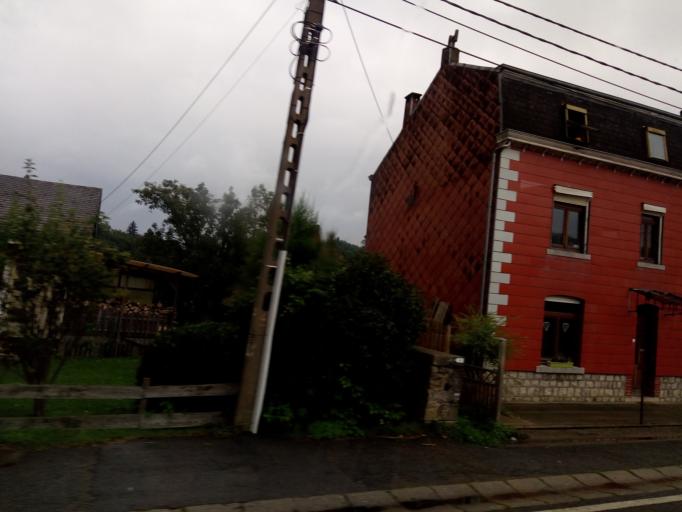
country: BE
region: Wallonia
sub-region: Province du Luxembourg
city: Hotton
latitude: 50.2591
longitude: 5.4692
